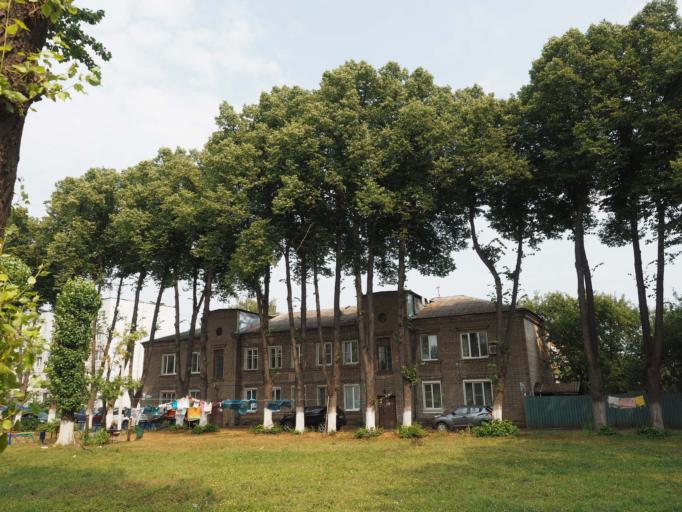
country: RU
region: Moskovskaya
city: Kraskovo
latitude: 55.6575
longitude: 37.9760
